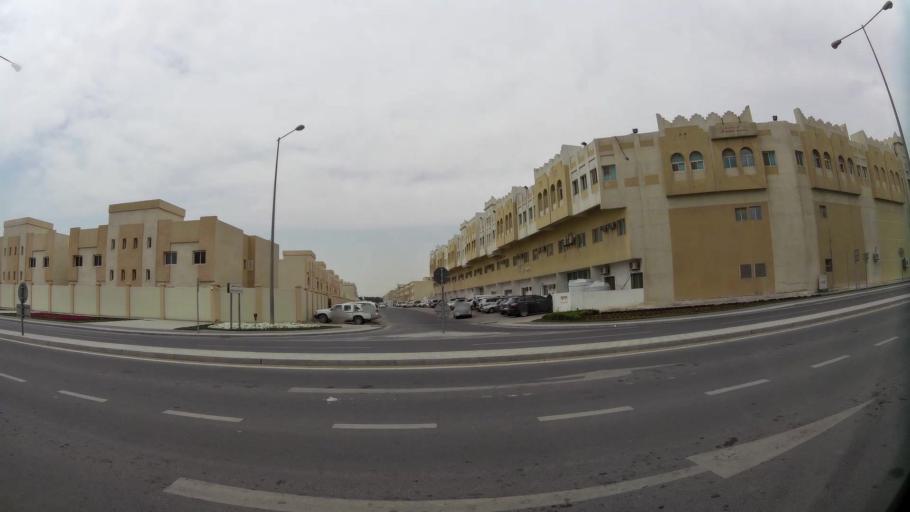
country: QA
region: Baladiyat ar Rayyan
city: Ar Rayyan
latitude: 25.2328
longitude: 51.4463
